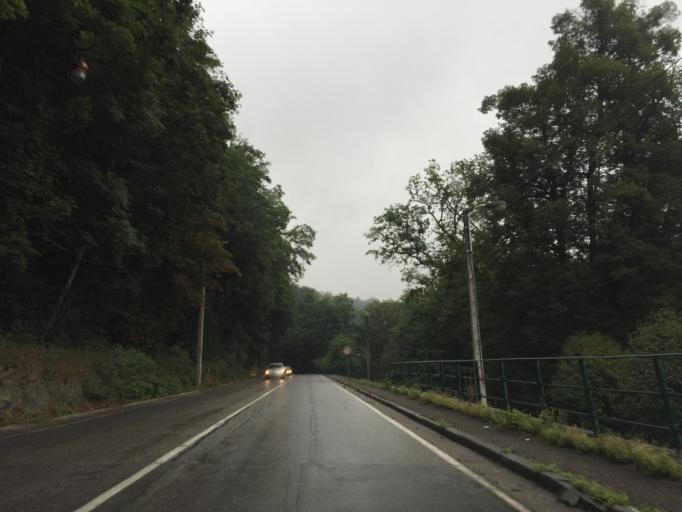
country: BE
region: Wallonia
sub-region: Province de Liege
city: Spa
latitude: 50.4933
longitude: 5.8735
